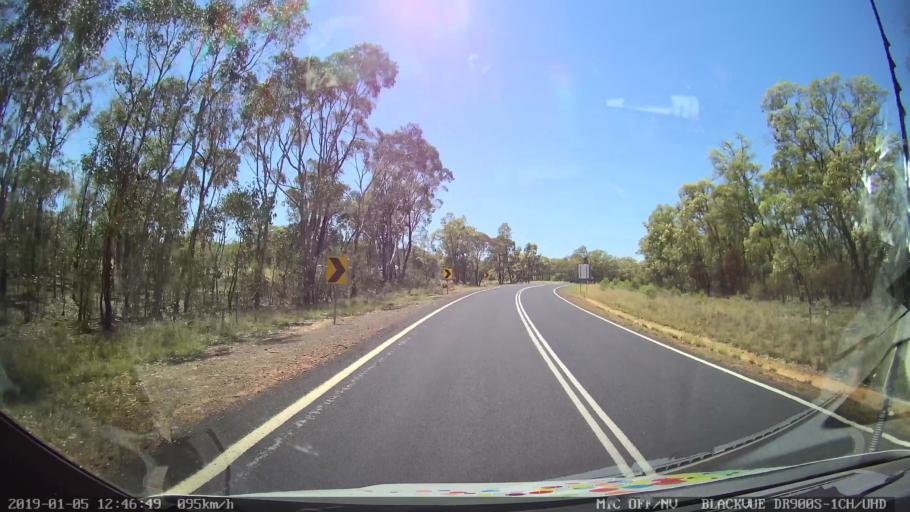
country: AU
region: New South Wales
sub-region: Warrumbungle Shire
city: Coonabarabran
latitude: -31.1146
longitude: 149.5676
